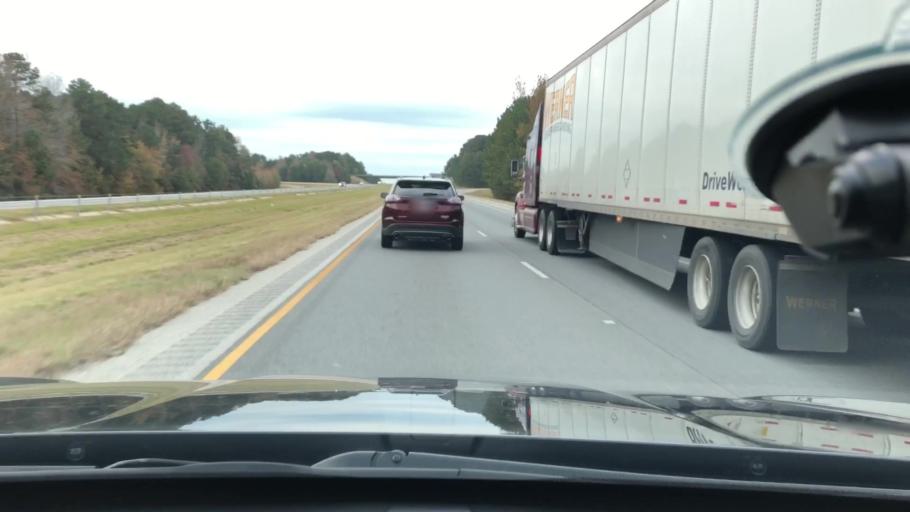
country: US
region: Arkansas
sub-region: Clark County
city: Arkadelphia
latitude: 34.0684
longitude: -93.1231
